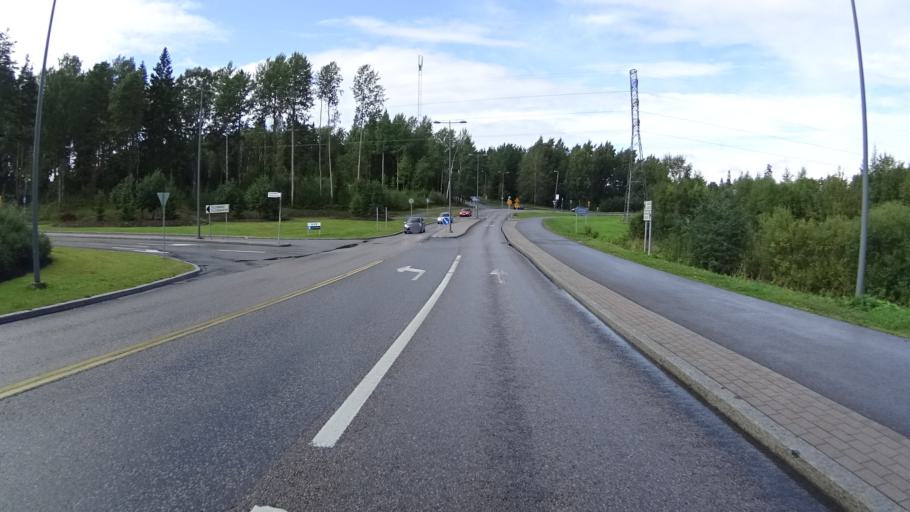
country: FI
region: Uusimaa
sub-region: Helsinki
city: Espoo
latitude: 60.1704
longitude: 24.6590
